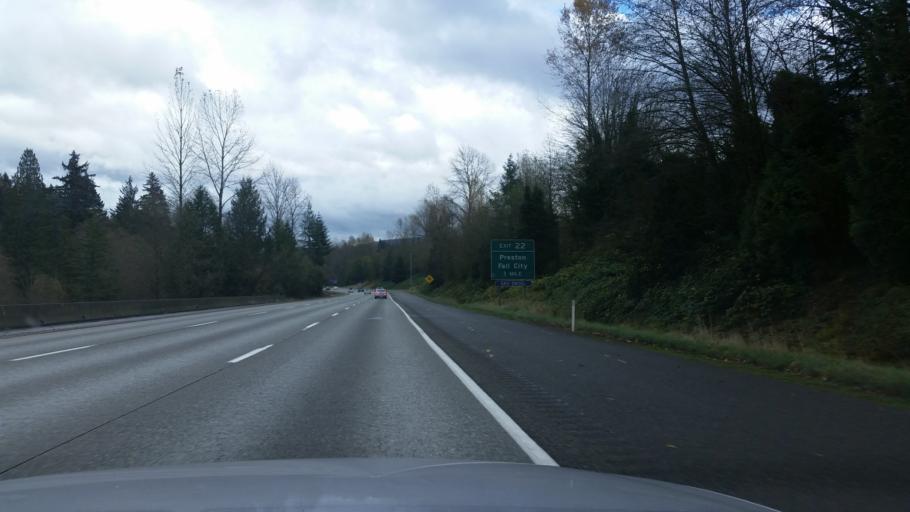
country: US
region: Washington
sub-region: King County
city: Issaquah
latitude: 47.5344
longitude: -121.9644
